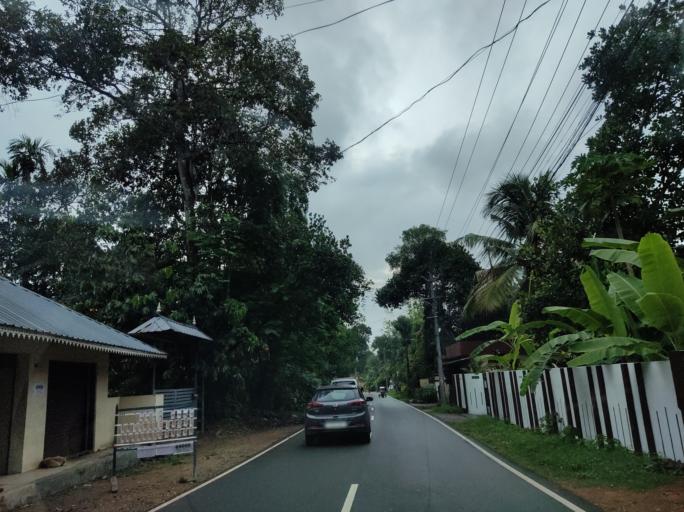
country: IN
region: Kerala
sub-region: Alappuzha
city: Mavelikara
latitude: 9.2379
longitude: 76.5547
